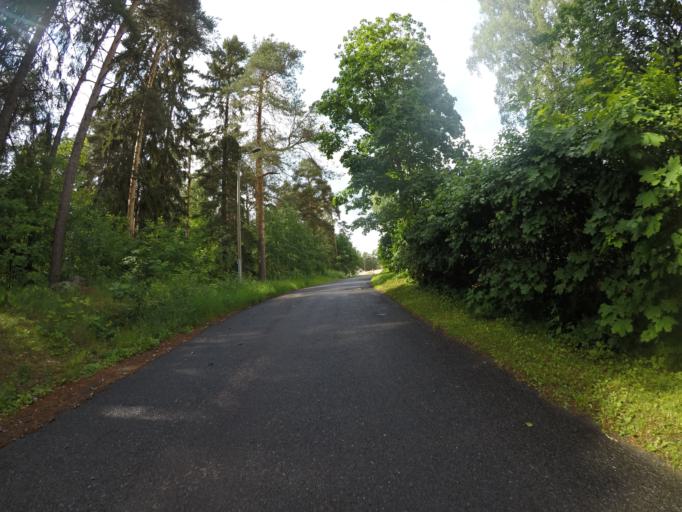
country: FI
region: Haeme
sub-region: Haemeenlinna
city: Haemeenlinna
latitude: 61.0065
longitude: 24.4732
